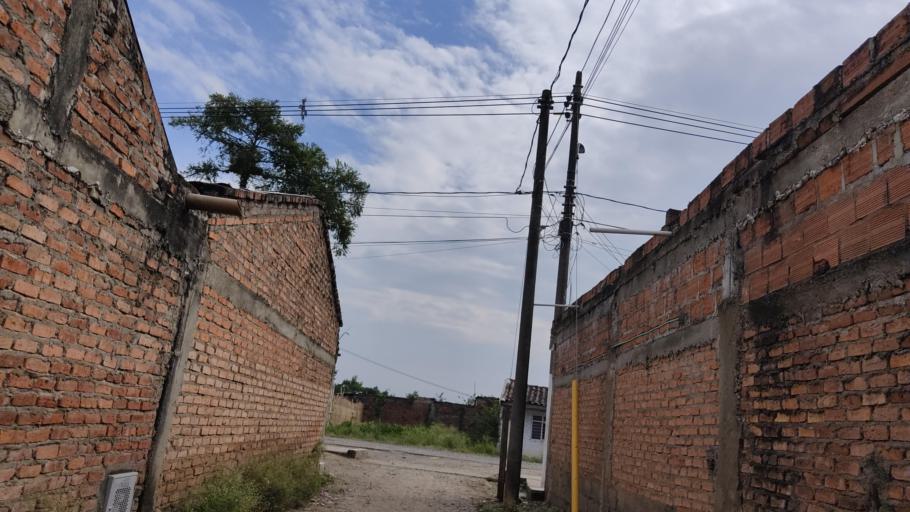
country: CO
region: Valle del Cauca
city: Jamundi
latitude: 3.1277
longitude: -76.5550
